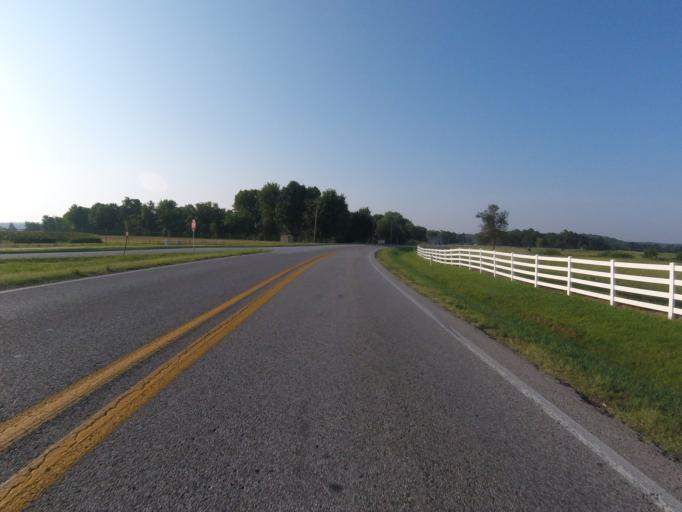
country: US
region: Arkansas
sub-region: Washington County
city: Fayetteville
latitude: 36.0931
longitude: -94.1750
